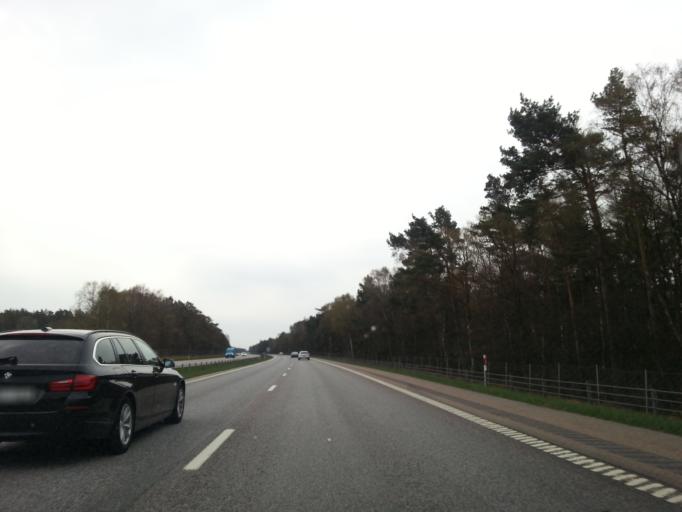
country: SE
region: Halland
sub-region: Halmstads Kommun
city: Paarp
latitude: 56.5666
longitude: 12.9509
